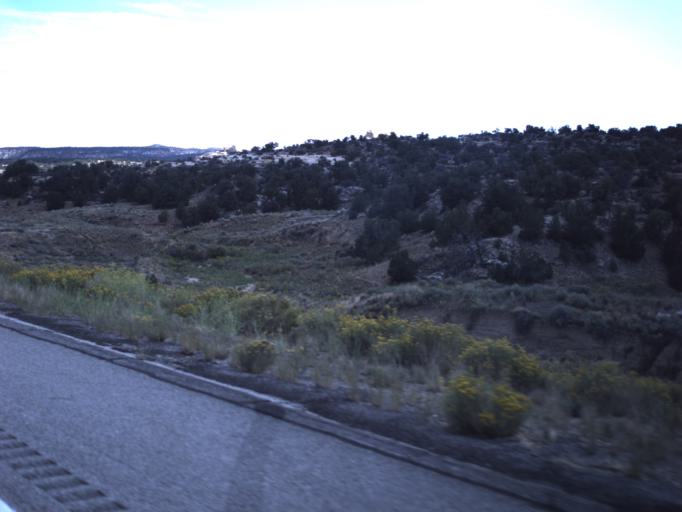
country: US
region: Utah
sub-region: Emery County
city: Ferron
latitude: 38.8655
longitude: -110.8009
